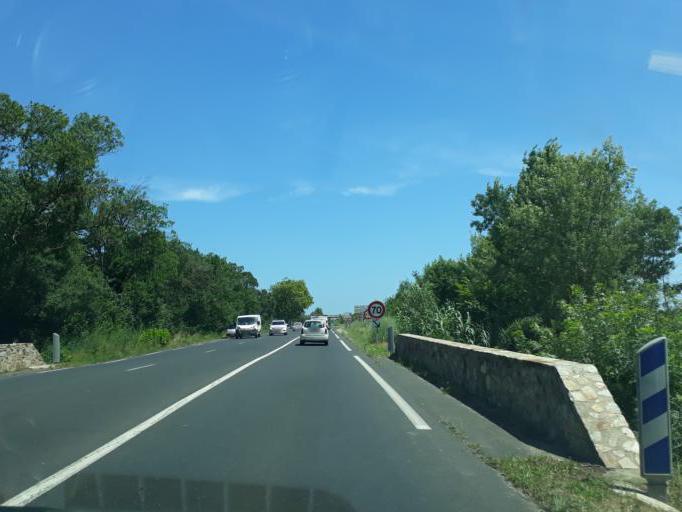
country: FR
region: Languedoc-Roussillon
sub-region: Departement de l'Herault
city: Vias
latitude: 43.3122
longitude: 3.3944
